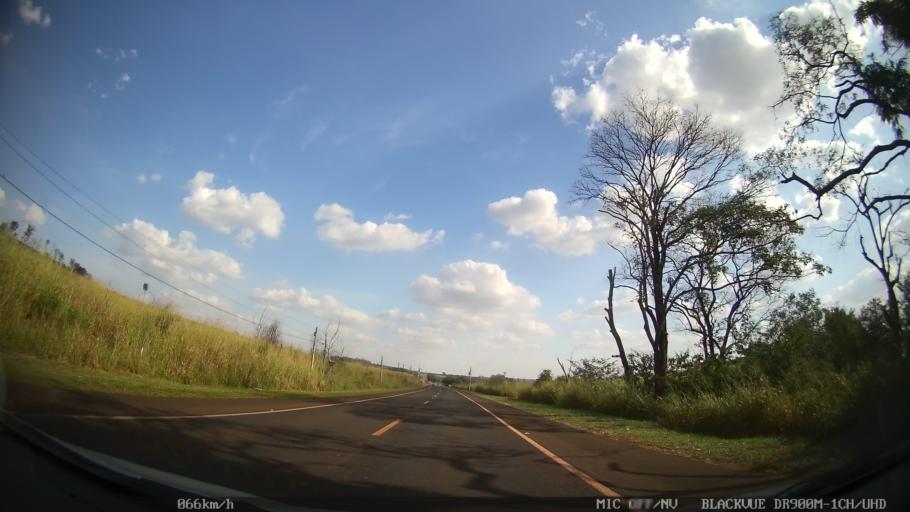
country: BR
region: Sao Paulo
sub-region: Ribeirao Preto
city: Ribeirao Preto
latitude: -21.1834
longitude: -47.8601
